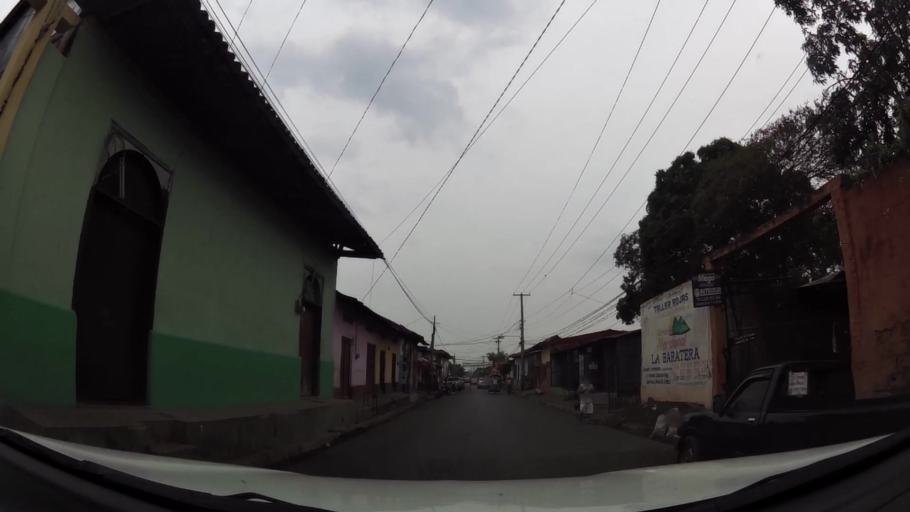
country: NI
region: Leon
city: Leon
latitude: 12.4441
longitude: -86.8738
